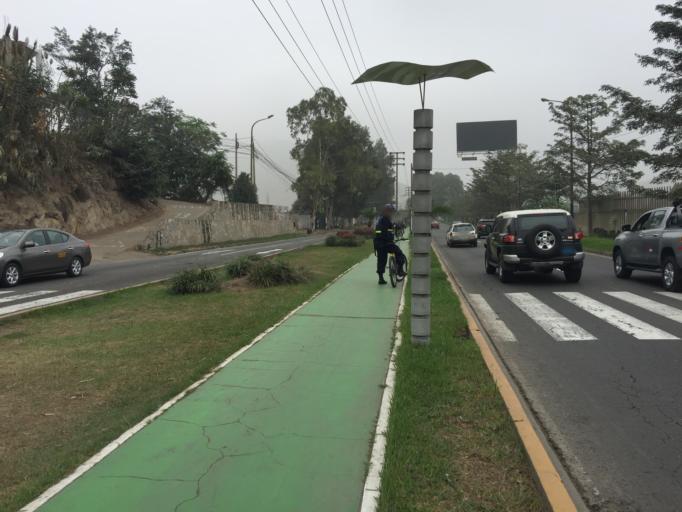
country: PE
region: Lima
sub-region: Lima
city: La Molina
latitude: -12.0882
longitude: -76.9450
